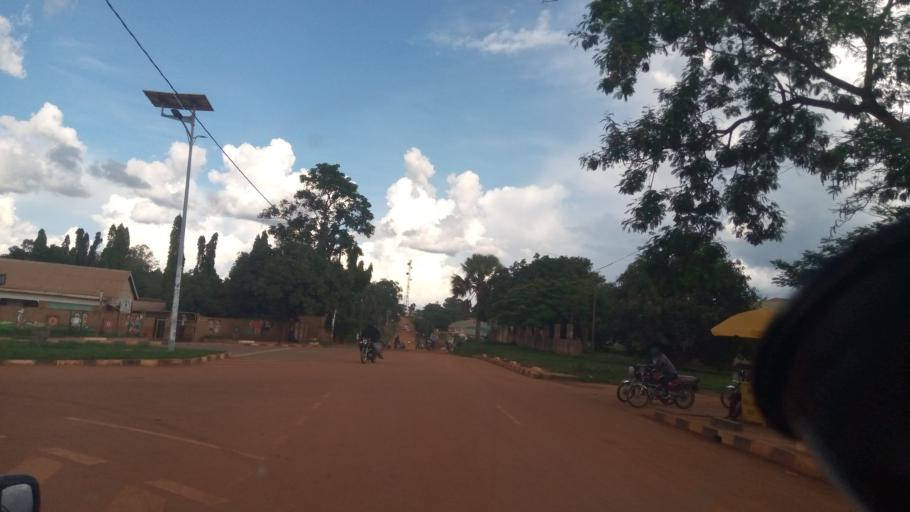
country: UG
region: Northern Region
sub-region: Lira District
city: Lira
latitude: 2.2390
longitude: 32.8991
